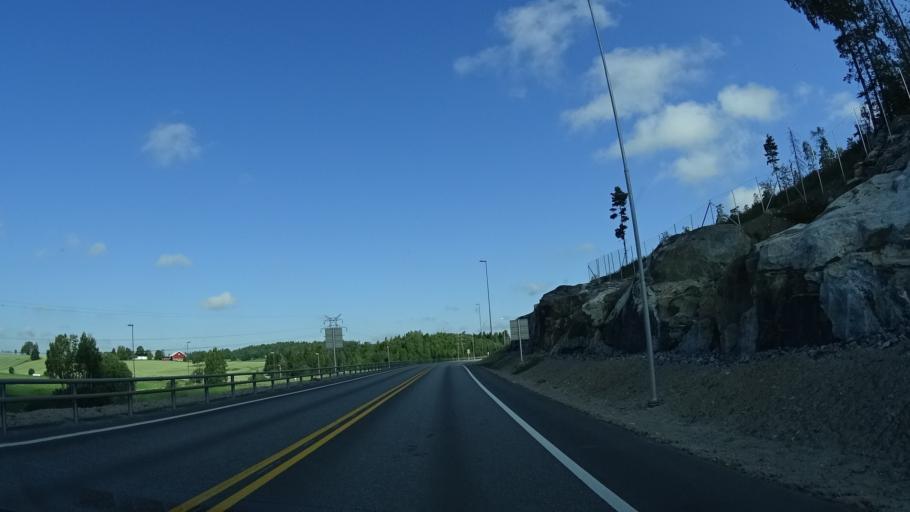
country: NO
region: Ostfold
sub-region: Hobol
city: Elvestad
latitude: 59.6454
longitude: 10.9258
